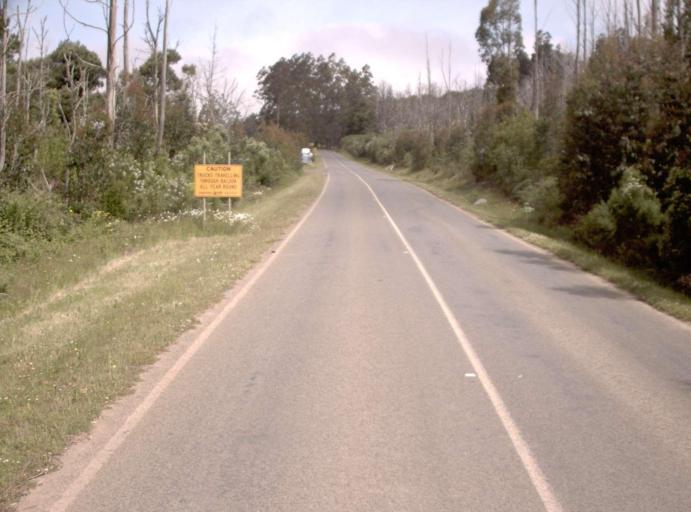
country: AU
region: Victoria
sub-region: Latrobe
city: Traralgon
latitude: -38.4136
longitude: 146.5659
